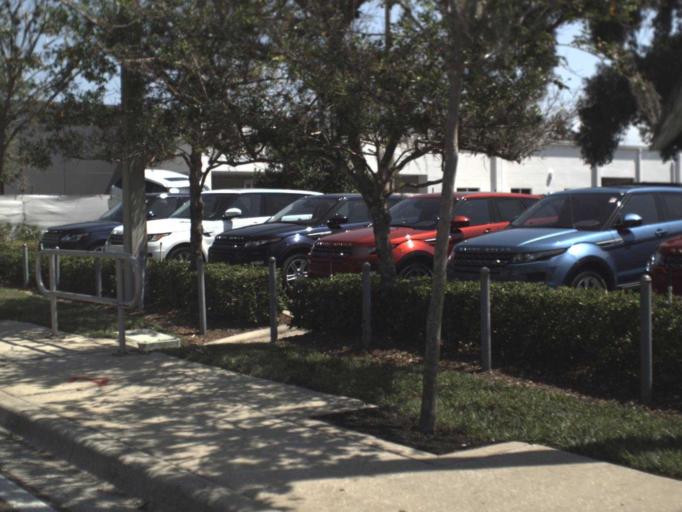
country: US
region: Florida
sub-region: Hillsborough County
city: Lake Magdalene
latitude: 28.0521
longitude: -82.4593
